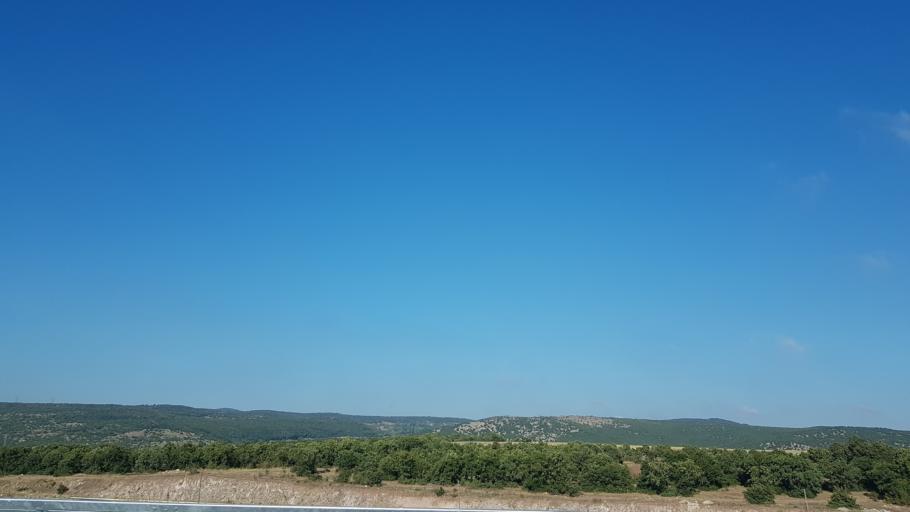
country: TR
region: Balikesir
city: Ertugrul
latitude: 39.5194
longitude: 27.6815
